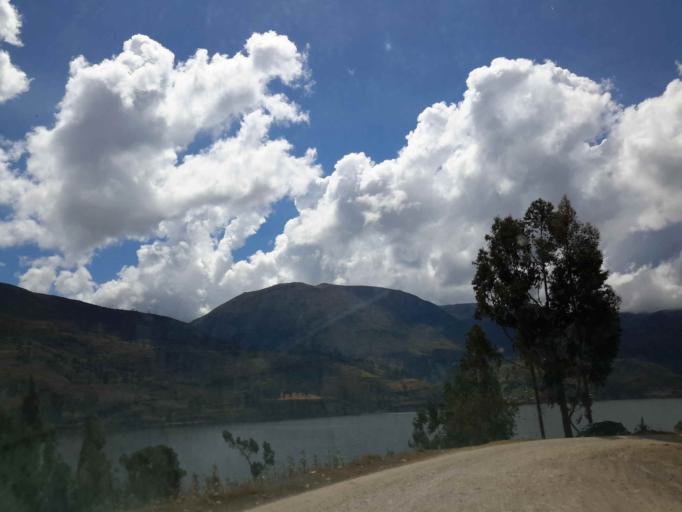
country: PE
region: Apurimac
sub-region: Provincia de Andahuaylas
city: Pacucha
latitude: -13.6177
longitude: -73.3338
